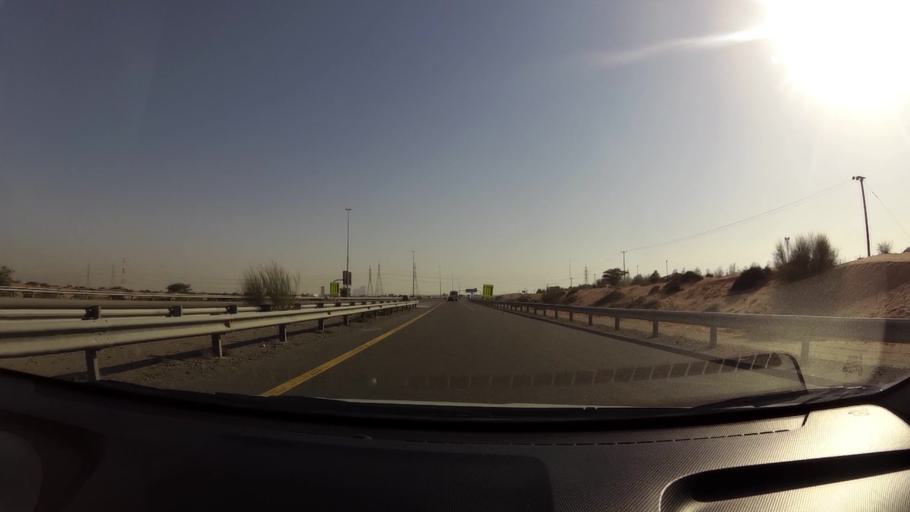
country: AE
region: Umm al Qaywayn
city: Umm al Qaywayn
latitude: 25.4452
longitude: 55.6079
